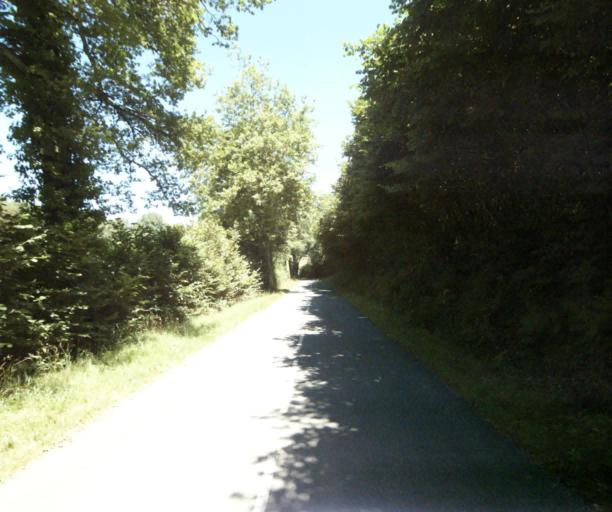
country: FR
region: Midi-Pyrenees
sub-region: Departement du Tarn
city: Dourgne
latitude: 43.4242
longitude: 2.1703
